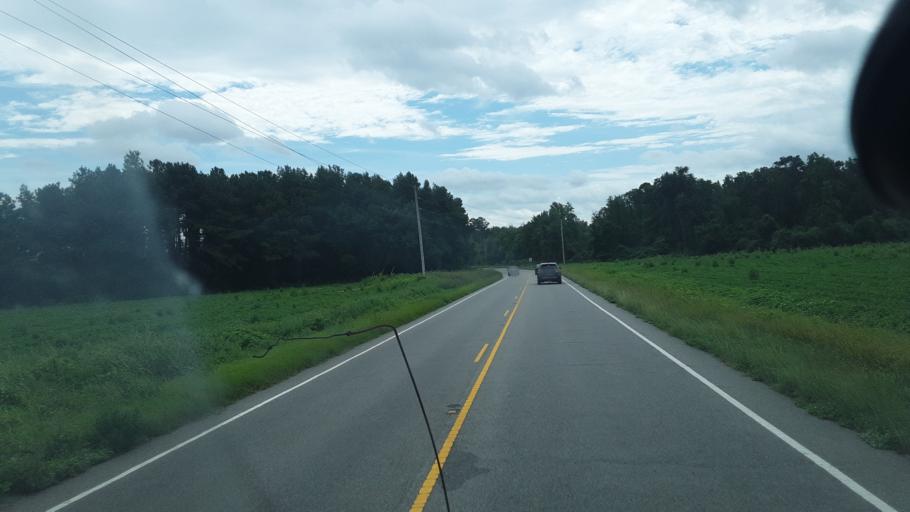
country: US
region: North Carolina
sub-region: Robeson County
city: Rowland
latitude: 34.5914
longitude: -79.3255
